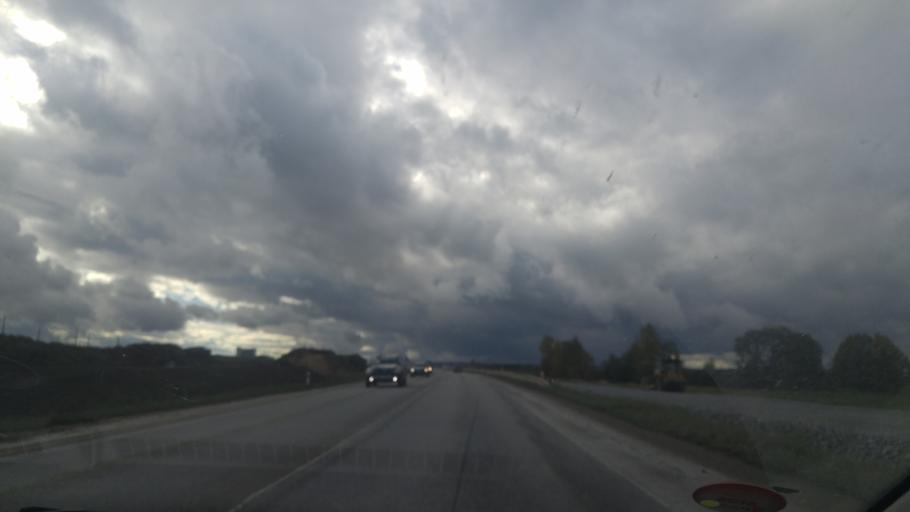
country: CZ
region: Jihocesky
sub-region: Okres Tabor
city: Veseli nad Luznici
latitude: 49.1598
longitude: 14.6431
